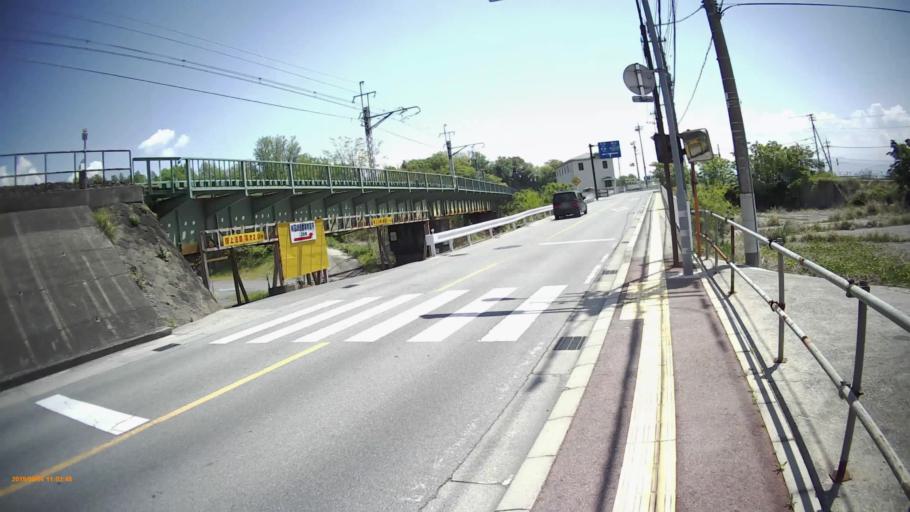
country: JP
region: Yamanashi
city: Nirasaki
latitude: 35.6988
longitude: 138.4653
